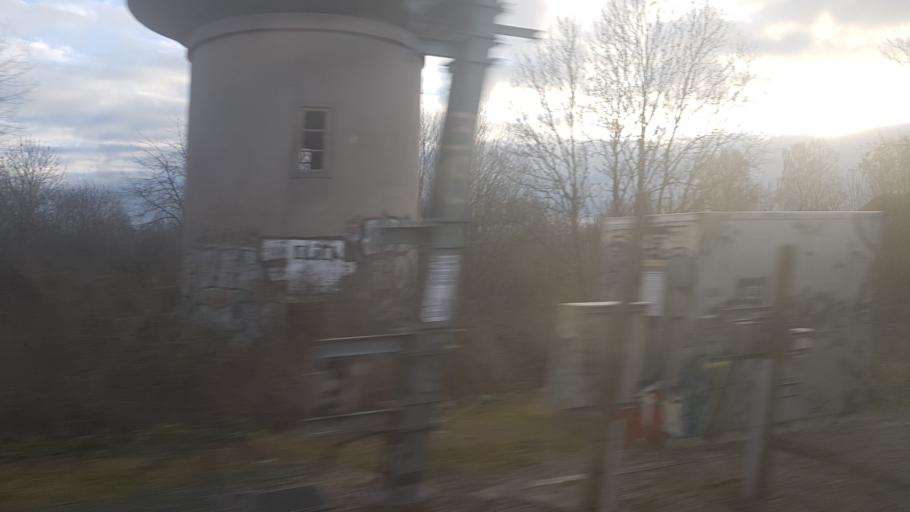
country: FR
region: Lorraine
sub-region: Departement des Vosges
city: Golbey
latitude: 48.2063
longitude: 6.4321
